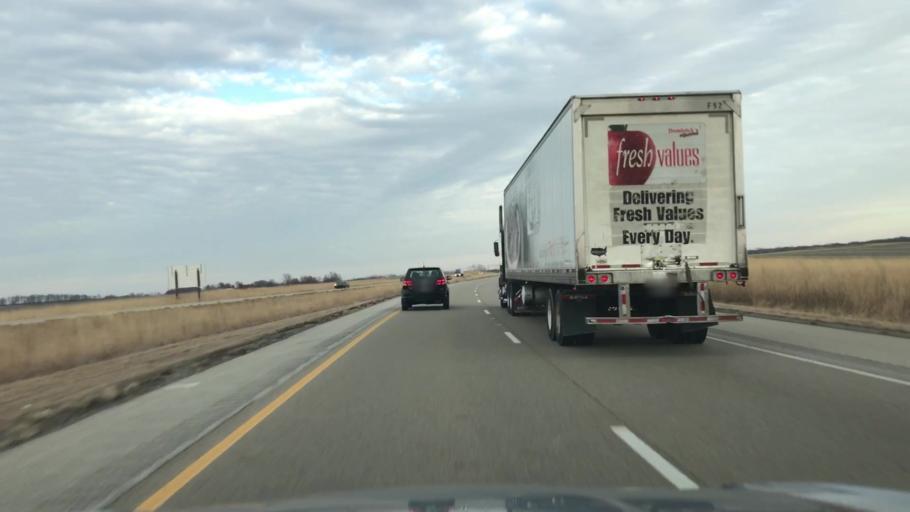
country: US
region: Illinois
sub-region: Logan County
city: Lincoln
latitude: 40.1812
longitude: -89.4049
